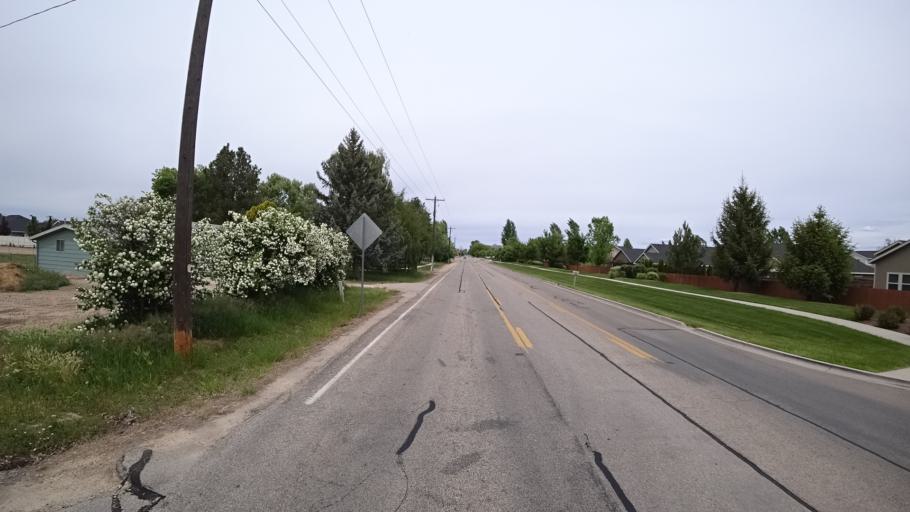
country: US
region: Idaho
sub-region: Ada County
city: Meridian
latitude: 43.5631
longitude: -116.3745
